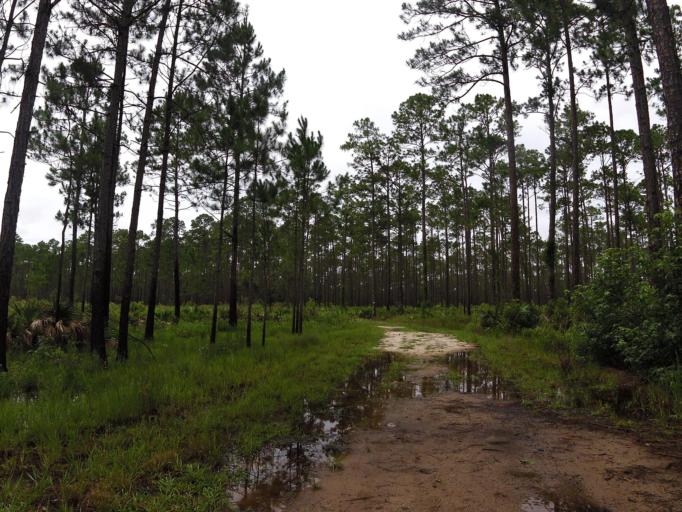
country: US
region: Florida
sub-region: Clay County
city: Green Cove Springs
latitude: 29.9684
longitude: -81.6293
